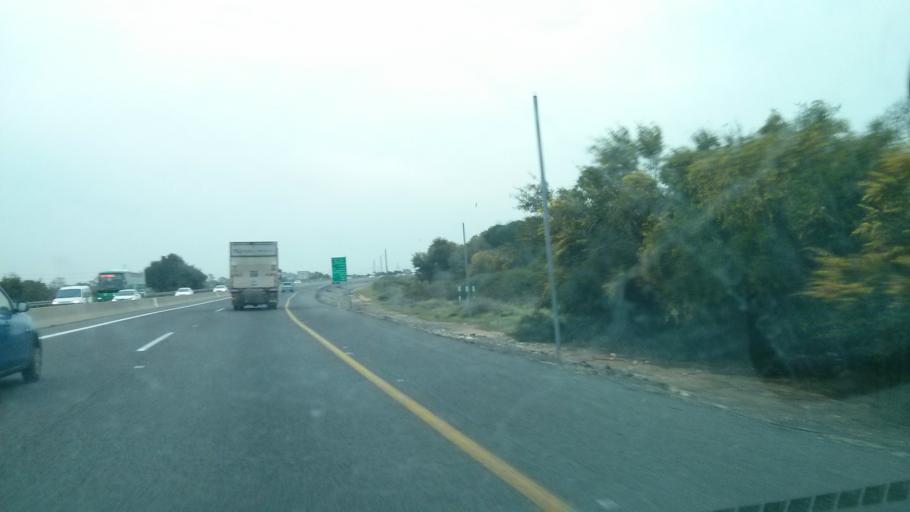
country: IL
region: Haifa
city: Qesarya
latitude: 32.4968
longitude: 34.9174
